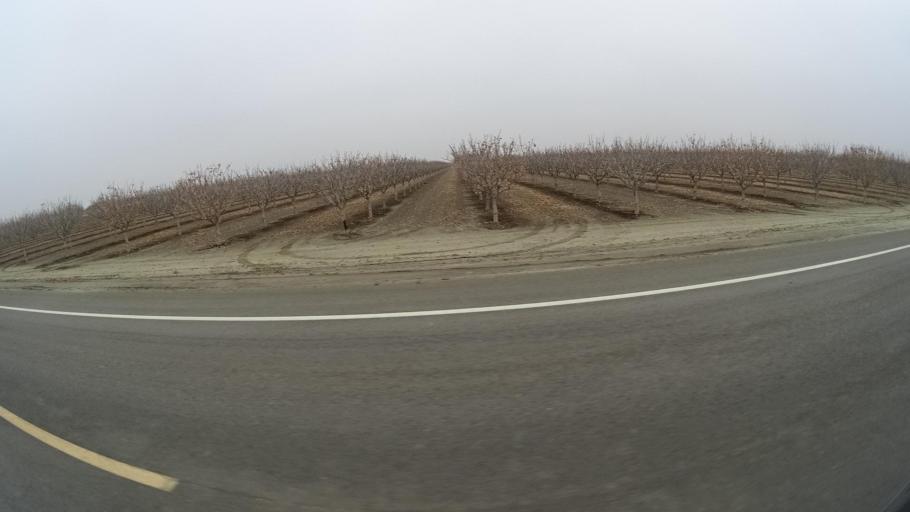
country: US
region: California
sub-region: Kern County
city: Buttonwillow
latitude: 35.3692
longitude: -119.4653
